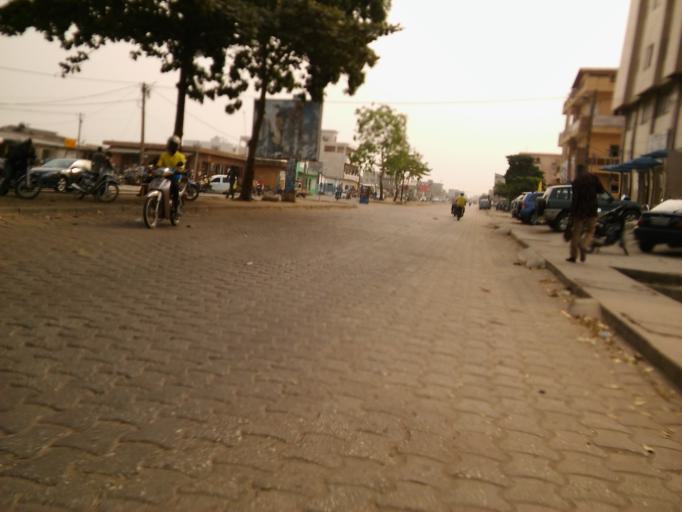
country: BJ
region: Littoral
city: Cotonou
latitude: 6.3778
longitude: 2.4078
